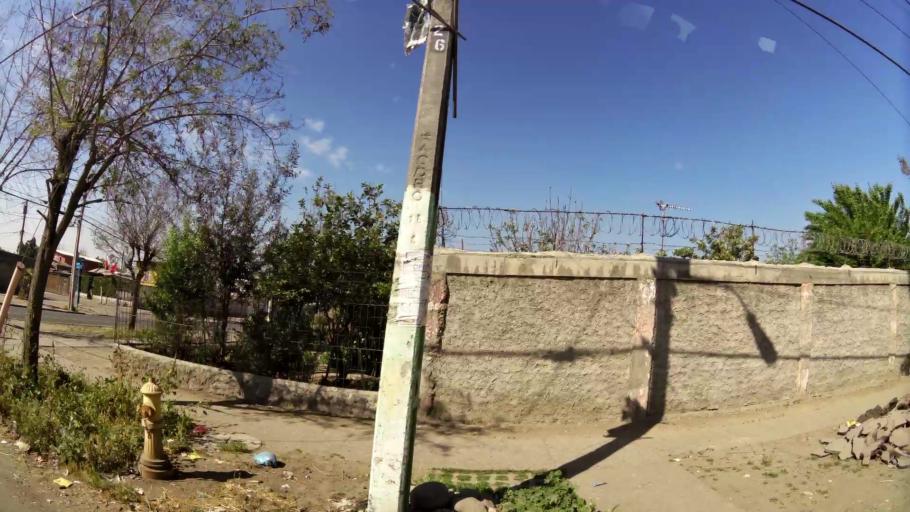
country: CL
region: Santiago Metropolitan
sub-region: Provincia de Santiago
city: La Pintana
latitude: -33.5377
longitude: -70.6122
